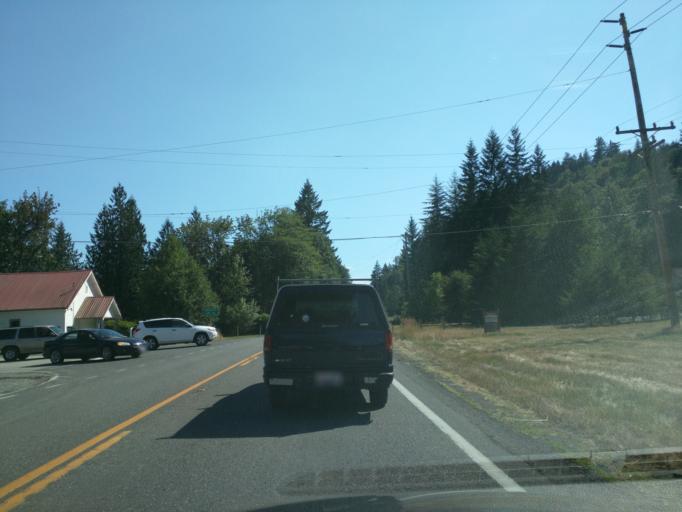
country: US
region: Washington
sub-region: Whatcom County
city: Peaceful Valley
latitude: 48.8383
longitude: -122.1671
